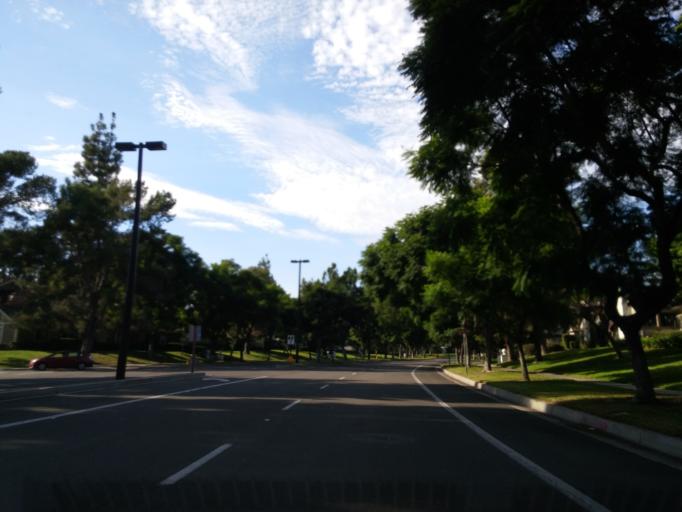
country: US
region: California
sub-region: Orange County
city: Irvine
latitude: 33.6694
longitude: -117.8128
